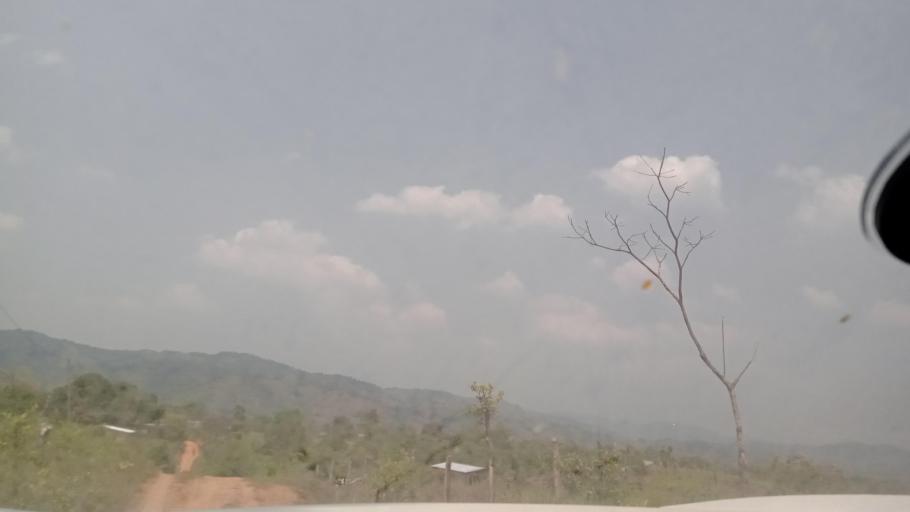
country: MX
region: Chiapas
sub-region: Tecpatan
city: Raudales Malpaso
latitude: 17.4675
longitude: -93.8266
